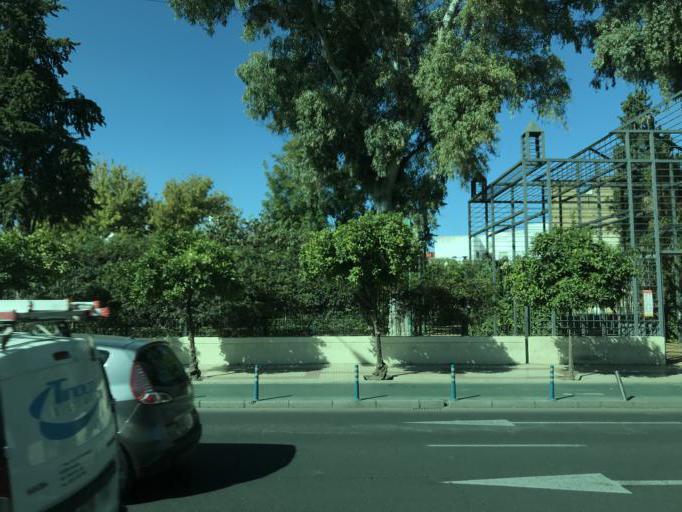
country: ES
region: Andalusia
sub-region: Provincia de Sevilla
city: Sevilla
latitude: 37.3958
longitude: -5.9825
